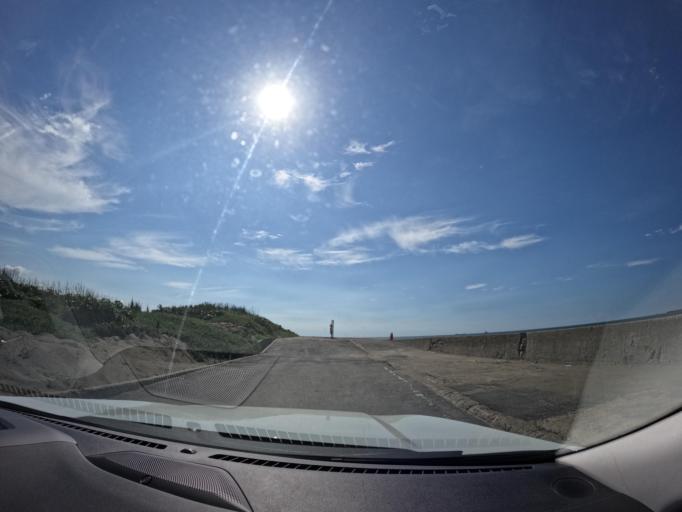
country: TW
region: Taiwan
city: Taoyuan City
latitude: 25.0934
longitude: 121.1884
